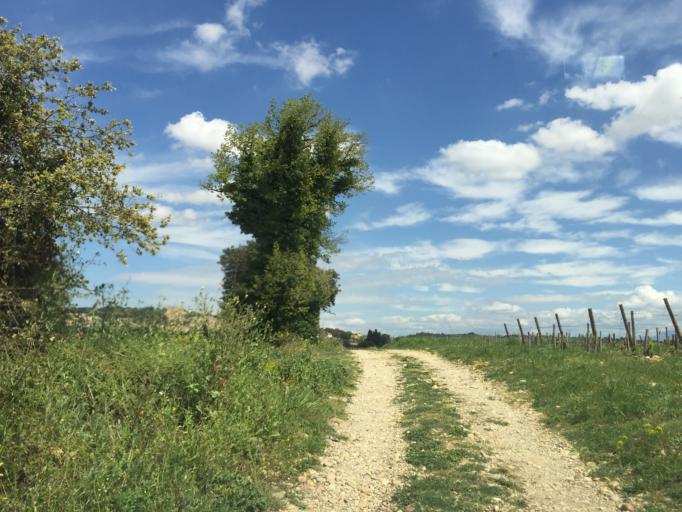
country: FR
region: Provence-Alpes-Cote d'Azur
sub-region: Departement du Vaucluse
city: Chateauneuf-du-Pape
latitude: 44.0458
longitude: 4.8219
